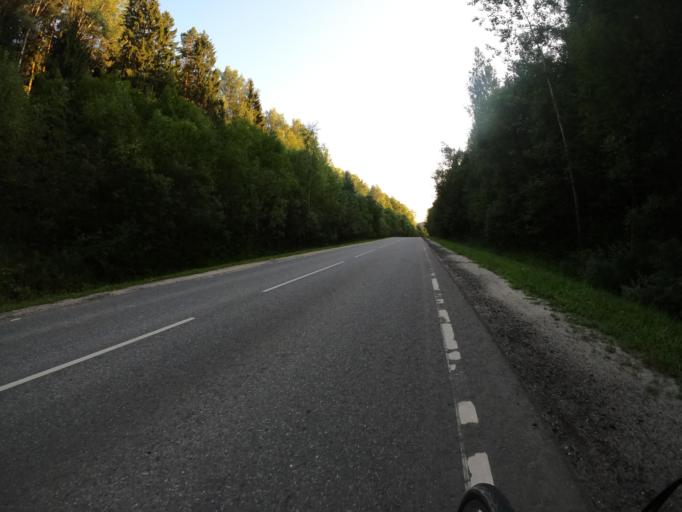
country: RU
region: Moskovskaya
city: Meshcherino
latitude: 55.1087
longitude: 38.3053
